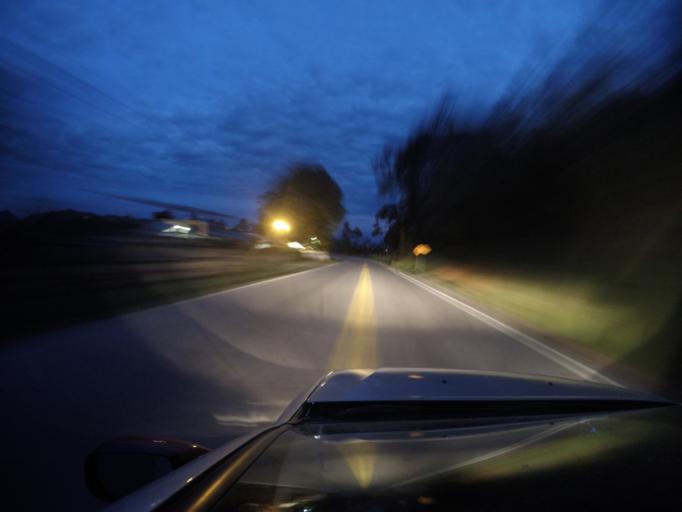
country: CO
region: Tolima
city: Fresno
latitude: 5.1575
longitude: -75.0776
